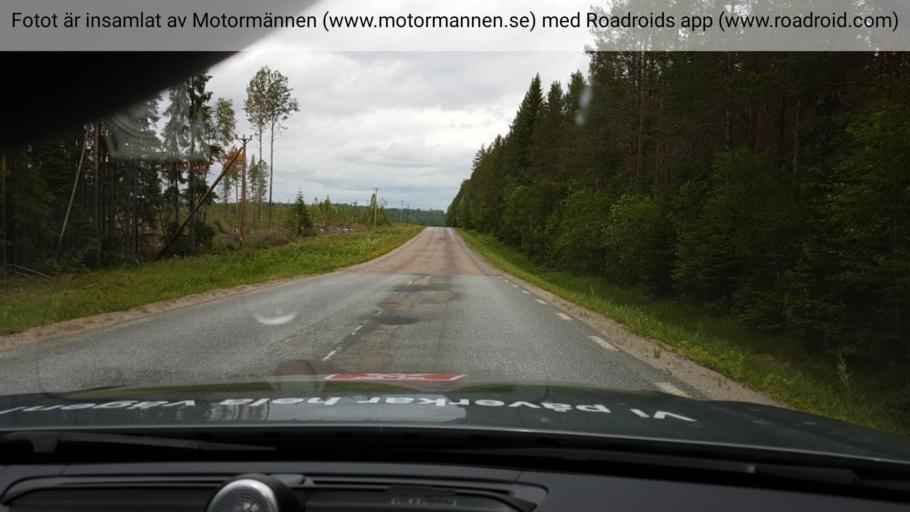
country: SE
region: Jaemtland
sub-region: Braecke Kommun
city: Braecke
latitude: 62.8229
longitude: 15.4613
